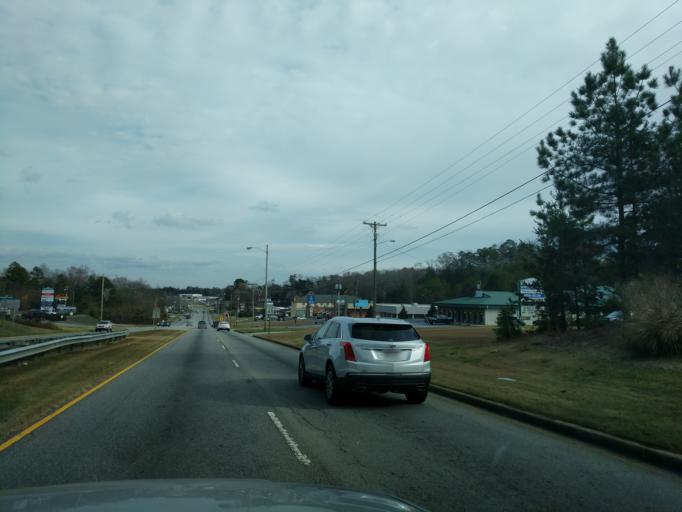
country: US
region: South Carolina
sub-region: Oconee County
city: Seneca
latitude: 34.6975
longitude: -82.9610
